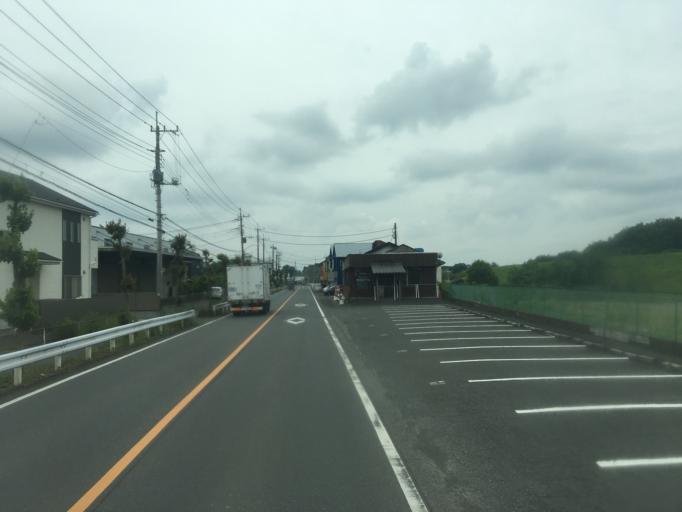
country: JP
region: Saitama
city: Kawagoe
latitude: 35.9733
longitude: 139.4621
